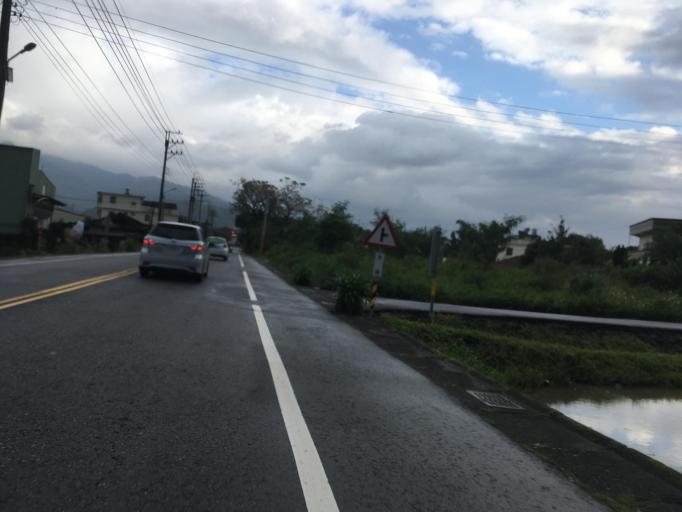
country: TW
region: Taiwan
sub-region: Yilan
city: Yilan
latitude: 24.8402
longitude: 121.8060
